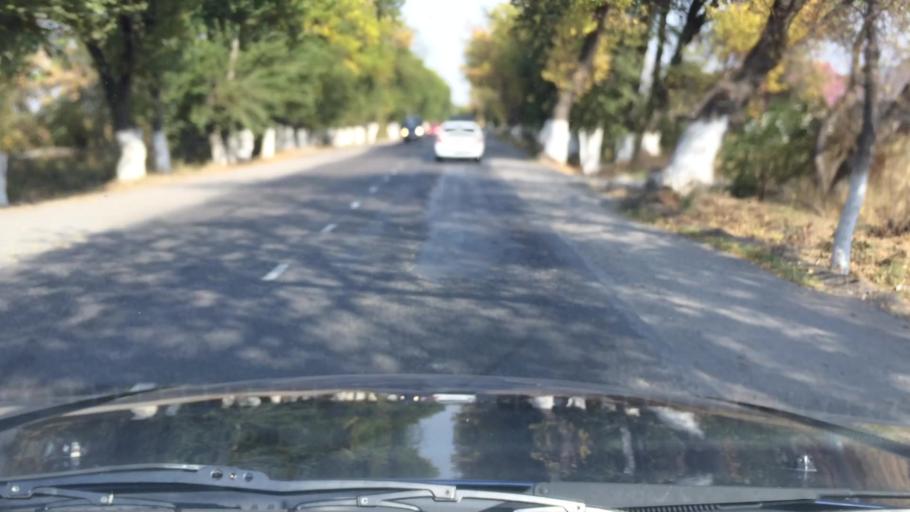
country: KG
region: Chuy
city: Lebedinovka
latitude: 42.9099
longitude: 74.6874
